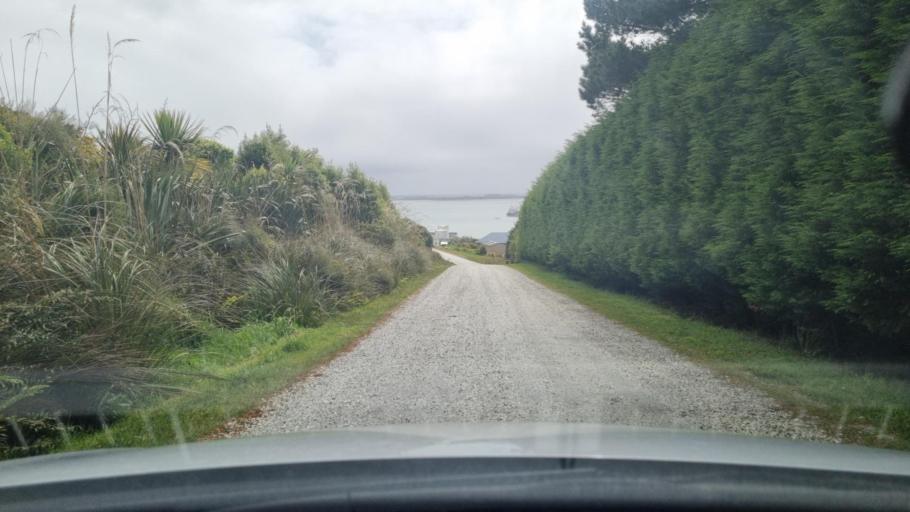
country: NZ
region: Southland
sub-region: Invercargill City
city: Bluff
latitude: -46.6097
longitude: 168.3520
